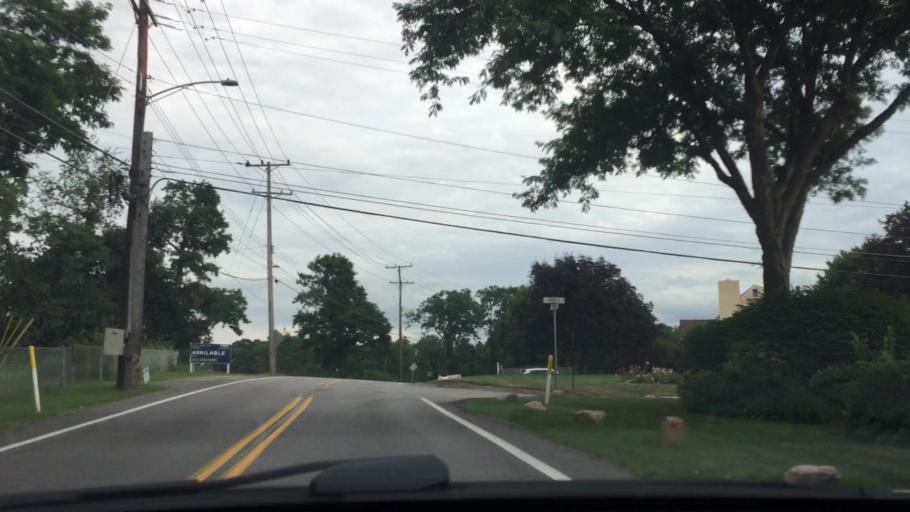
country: US
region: Pennsylvania
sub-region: Allegheny County
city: Castle Shannon
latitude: 40.3578
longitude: -80.0164
